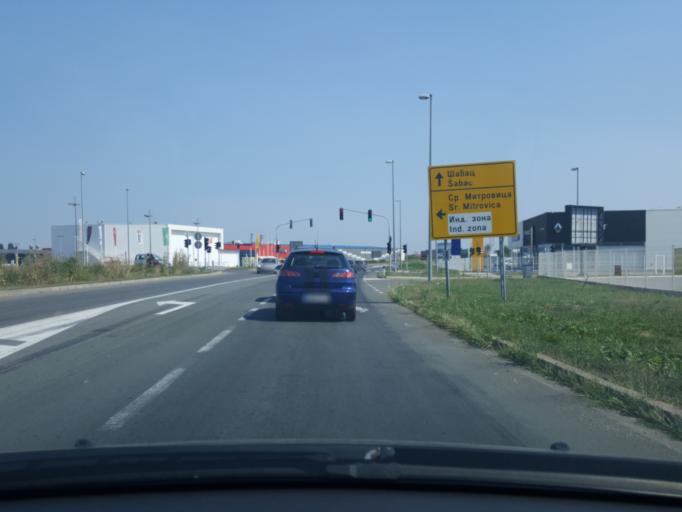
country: RS
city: Majur
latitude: 44.7544
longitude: 19.6602
